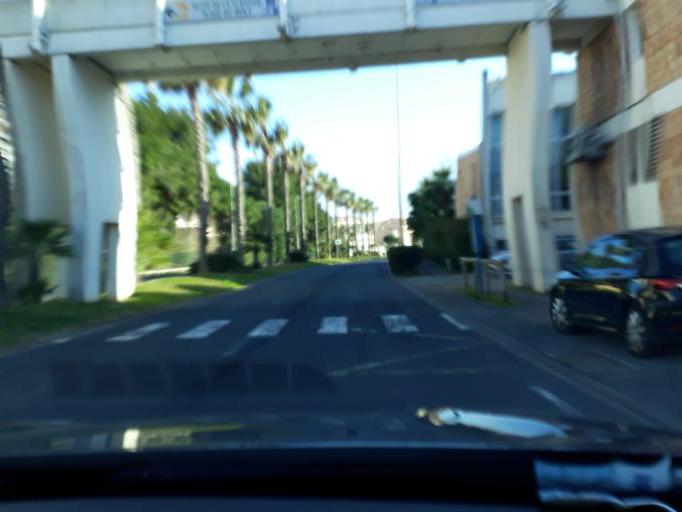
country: FR
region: Languedoc-Roussillon
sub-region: Departement de l'Herault
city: Le Cap d'Agde
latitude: 43.2841
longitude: 3.5150
